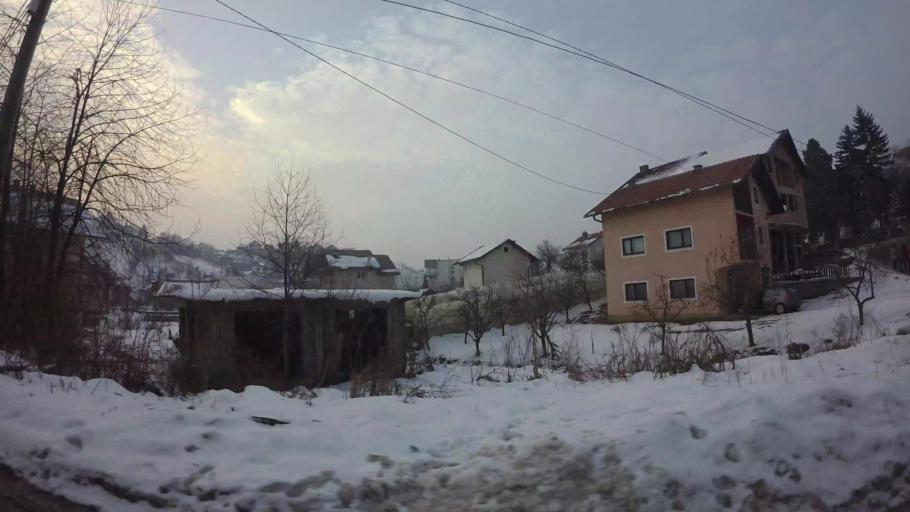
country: BA
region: Federation of Bosnia and Herzegovina
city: Hotonj
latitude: 43.8958
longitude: 18.3728
